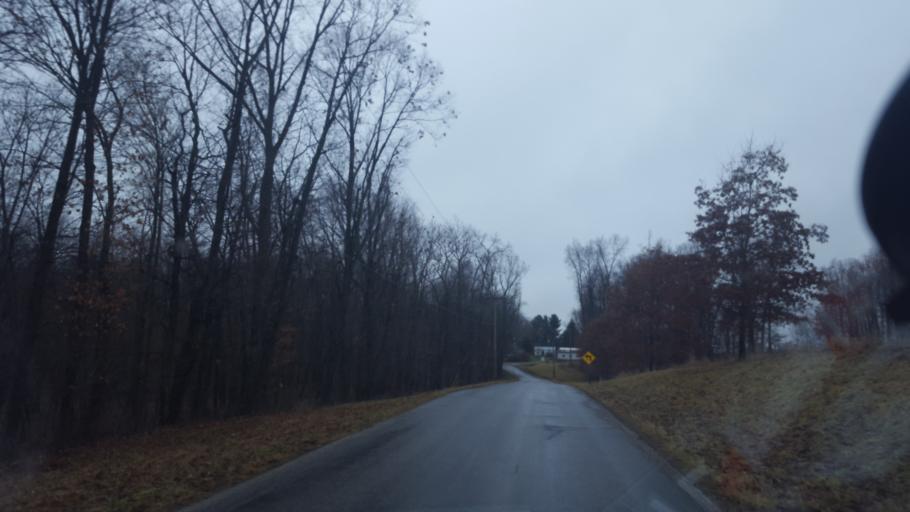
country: US
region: Ohio
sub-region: Ashland County
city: Loudonville
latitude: 40.5631
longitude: -82.3501
